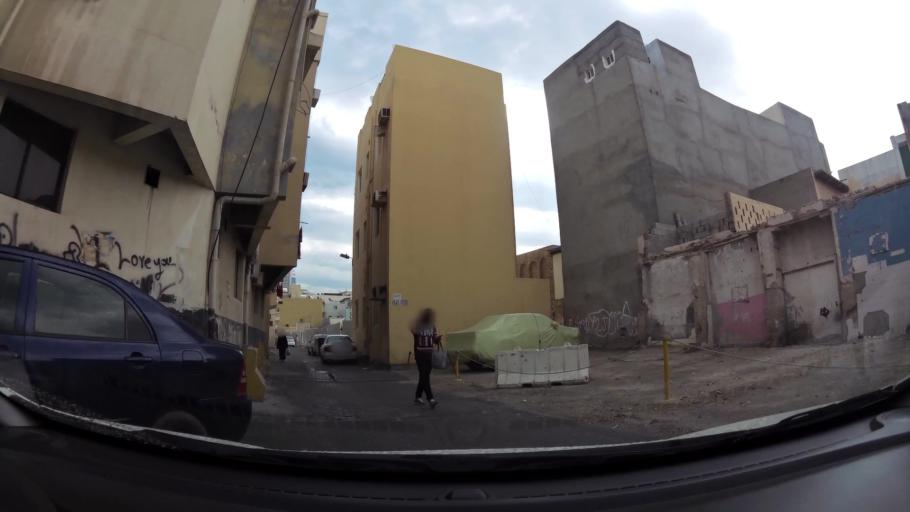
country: BH
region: Manama
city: Manama
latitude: 26.2308
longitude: 50.5930
